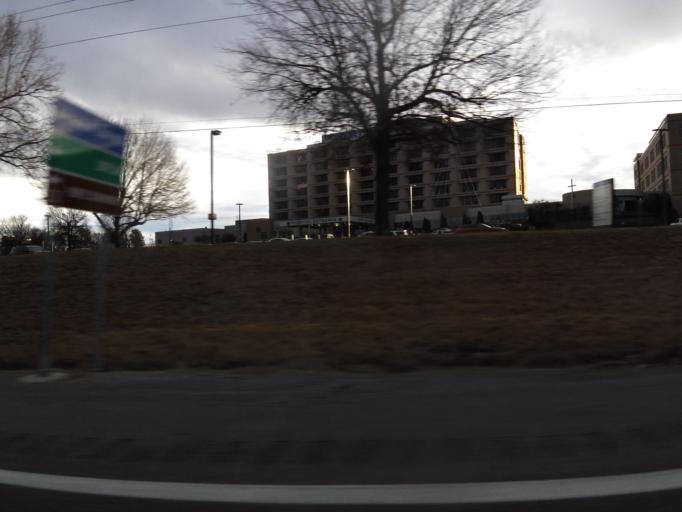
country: US
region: Kentucky
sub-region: McCracken County
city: Hendron
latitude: 37.0505
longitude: -88.6491
